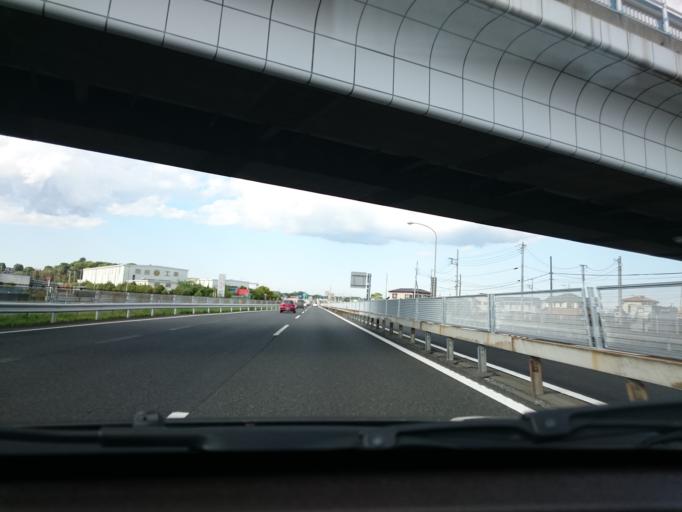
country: JP
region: Kanagawa
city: Isehara
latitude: 35.3653
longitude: 139.3081
